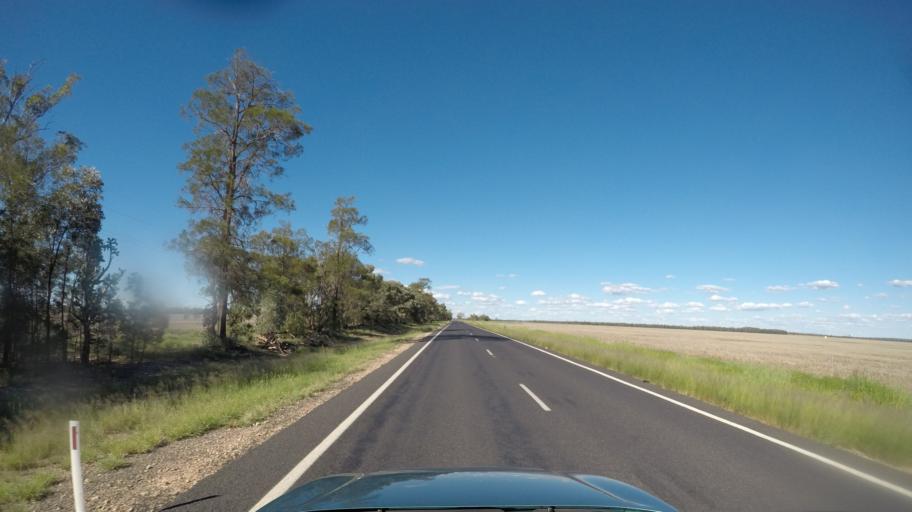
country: AU
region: Queensland
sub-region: Goondiwindi
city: Goondiwindi
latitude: -28.1463
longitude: 150.6860
